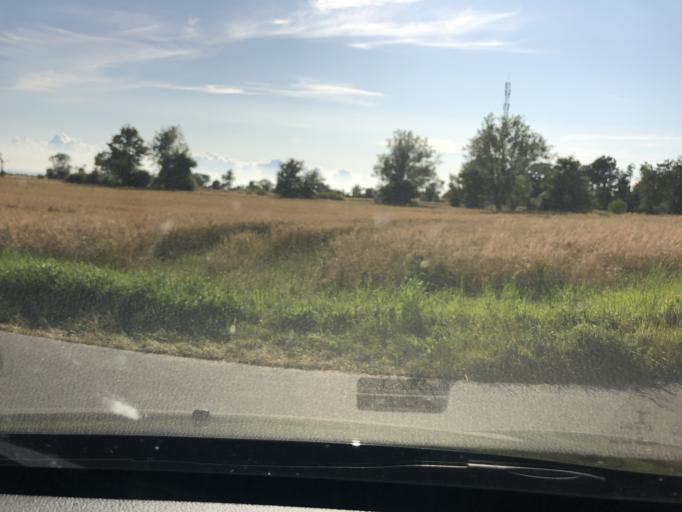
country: DK
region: South Denmark
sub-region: AEro Kommune
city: AEroskobing
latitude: 54.8608
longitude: 10.3813
